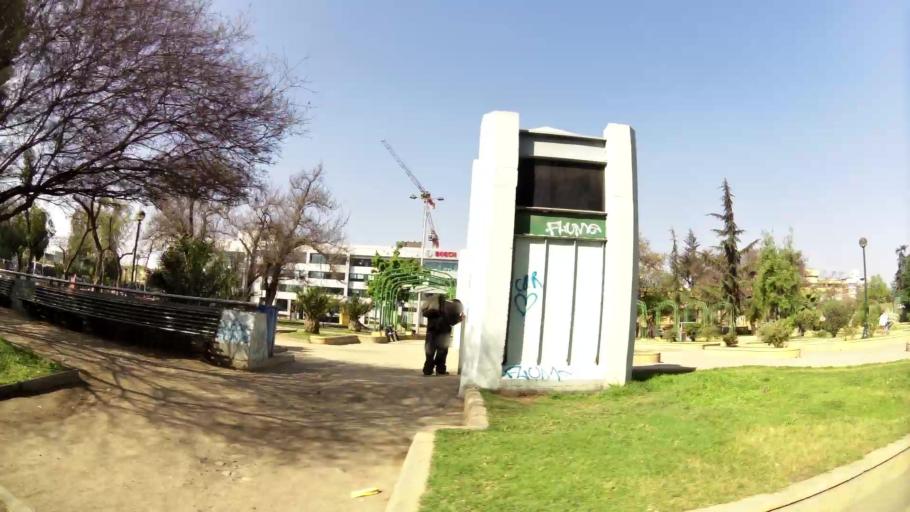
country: CL
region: Santiago Metropolitan
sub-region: Provincia de Santiago
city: Santiago
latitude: -33.4534
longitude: -70.6288
